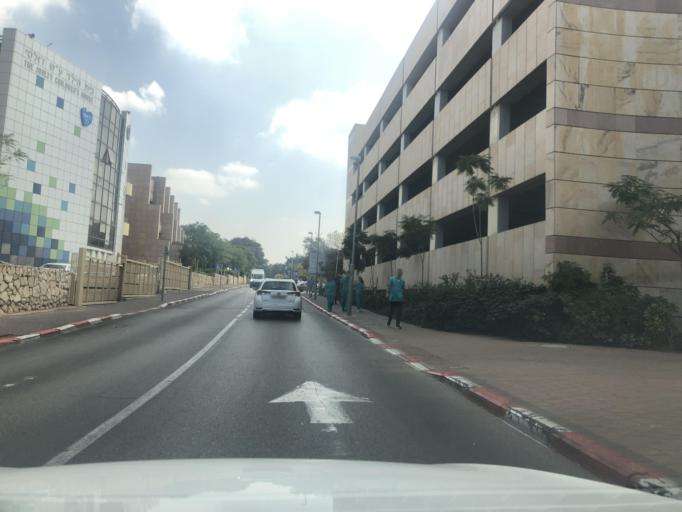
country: IL
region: Tel Aviv
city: Or Yehuda
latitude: 32.0473
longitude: 34.8452
